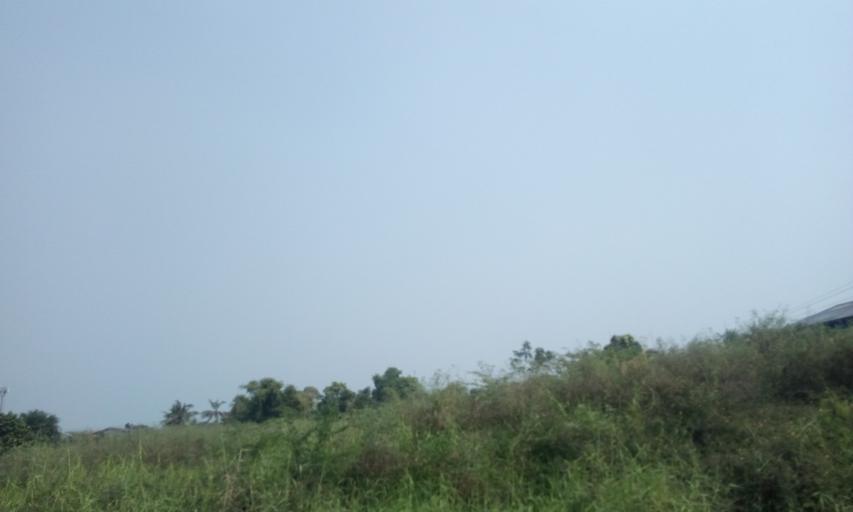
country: TH
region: Pathum Thani
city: Lam Luk Ka
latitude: 13.9477
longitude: 100.7247
